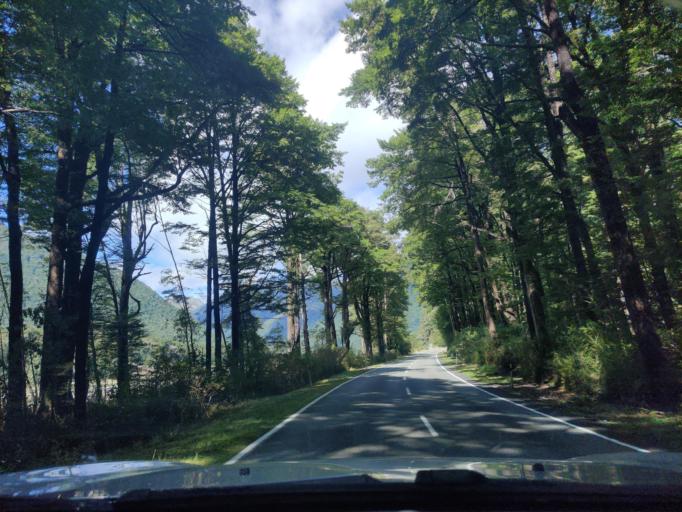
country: NZ
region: West Coast
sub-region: Buller District
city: Westport
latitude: -42.3678
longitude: 172.2631
